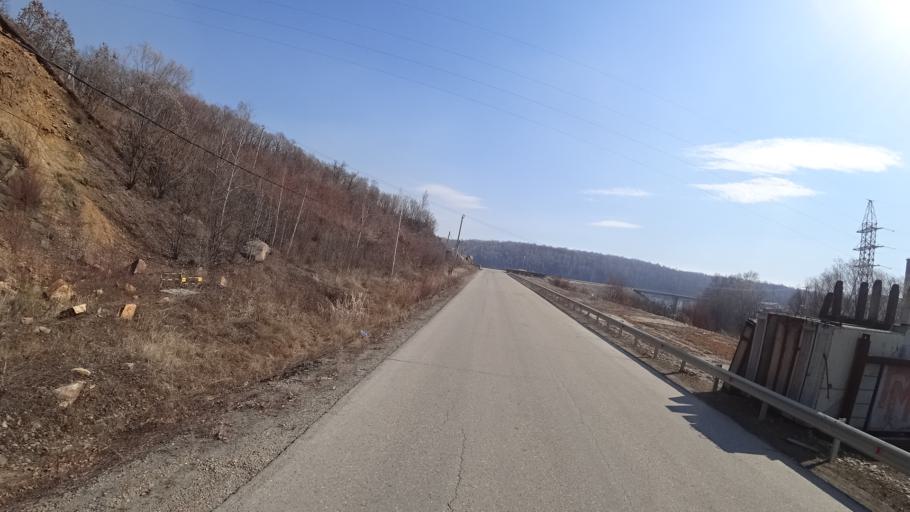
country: RU
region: Amur
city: Novobureyskiy
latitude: 49.7917
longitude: 129.9644
